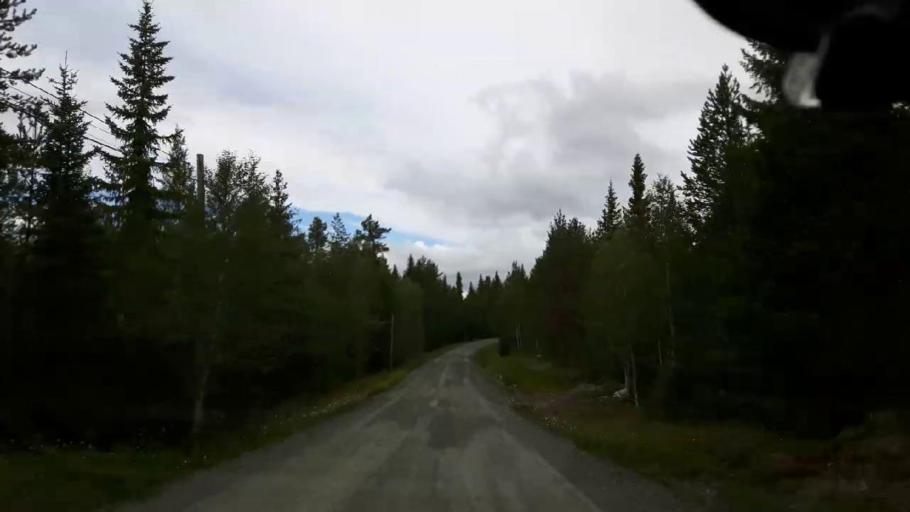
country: SE
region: Jaemtland
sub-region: Krokoms Kommun
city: Valla
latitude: 63.6892
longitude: 13.8693
